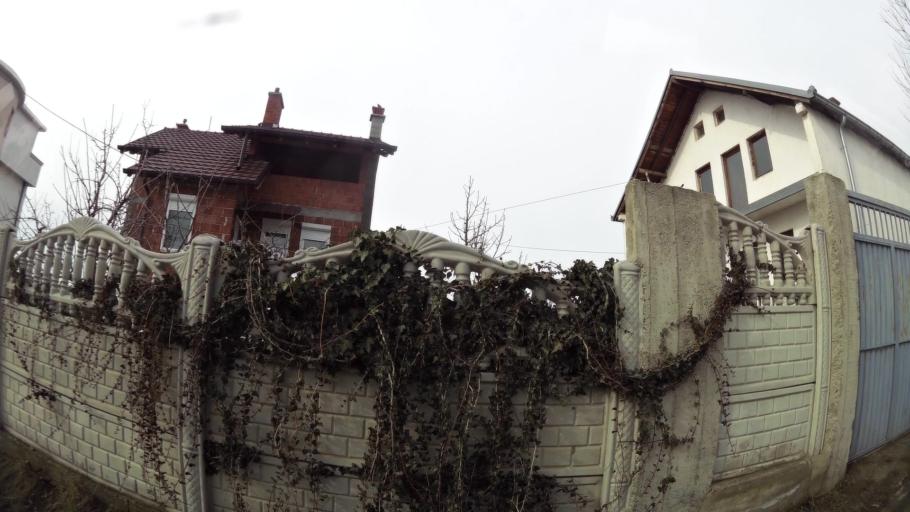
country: XK
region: Pristina
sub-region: Komuna e Prishtines
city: Pristina
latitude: 42.6914
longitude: 21.1688
